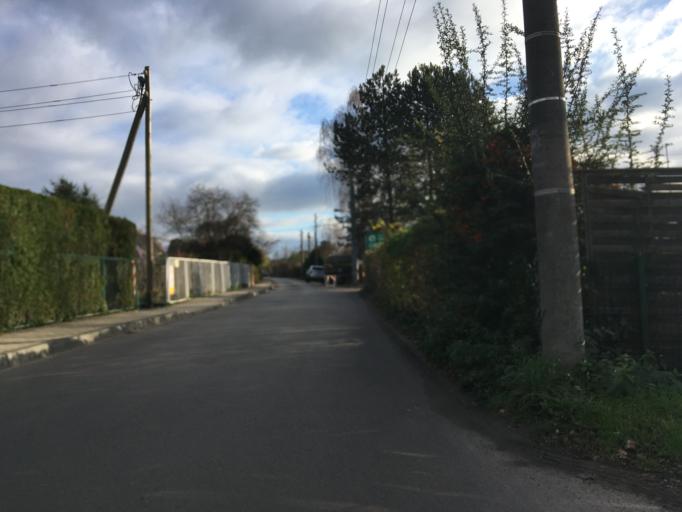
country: DE
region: Berlin
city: Baumschulenweg
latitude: 52.4485
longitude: 13.4733
